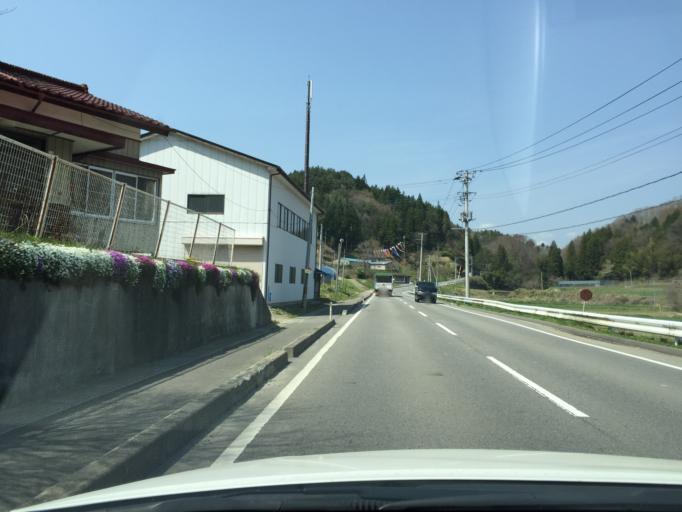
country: JP
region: Fukushima
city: Funehikimachi-funehiki
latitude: 37.4455
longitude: 140.6706
